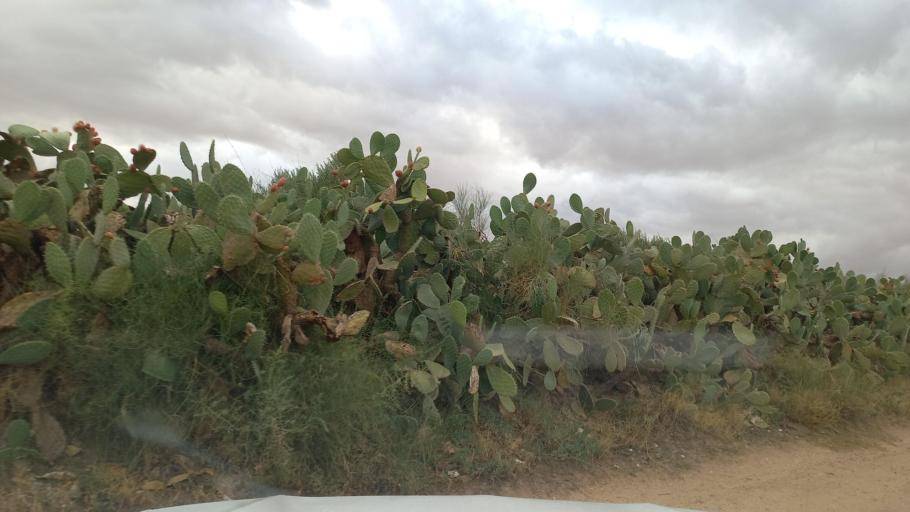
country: TN
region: Al Qasrayn
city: Kasserine
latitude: 35.2755
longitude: 8.9479
